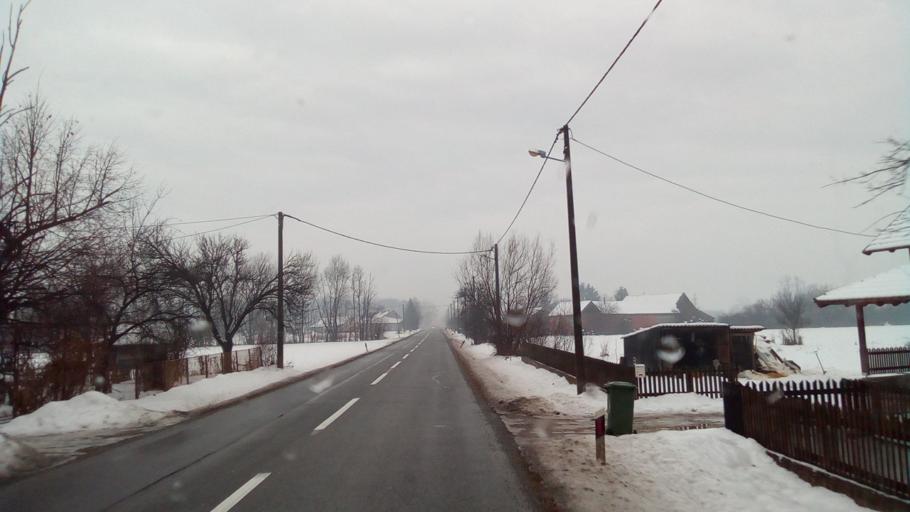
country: HR
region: Sisacko-Moslavacka
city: Petrinja
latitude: 45.4709
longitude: 16.2549
